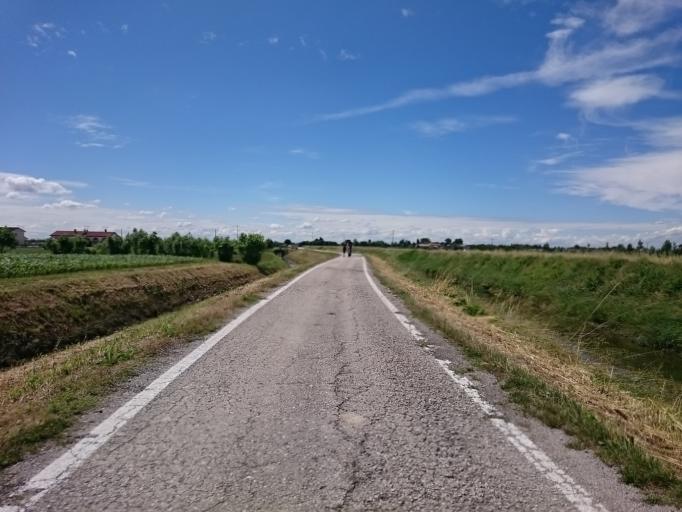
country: IT
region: Veneto
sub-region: Provincia di Padova
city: Legnaro
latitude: 45.3374
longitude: 11.9467
